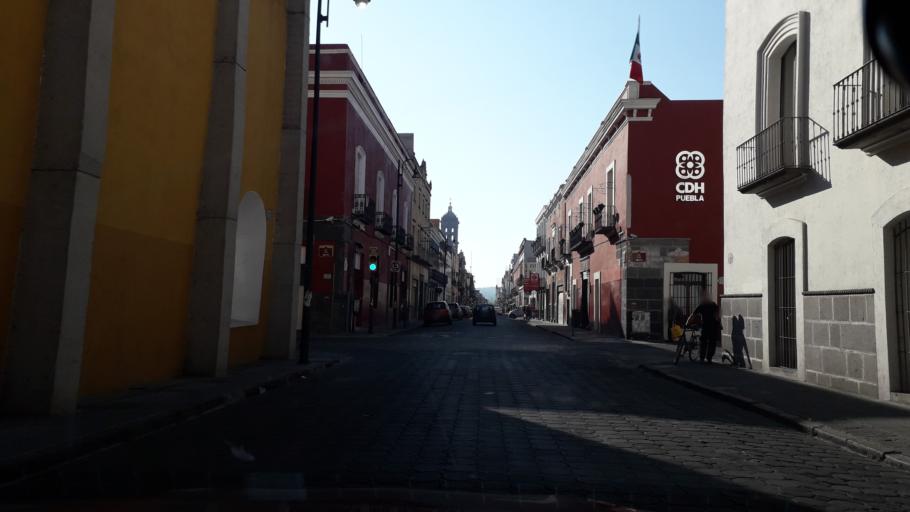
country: MX
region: Puebla
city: Puebla
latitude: 19.0446
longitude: -98.2028
